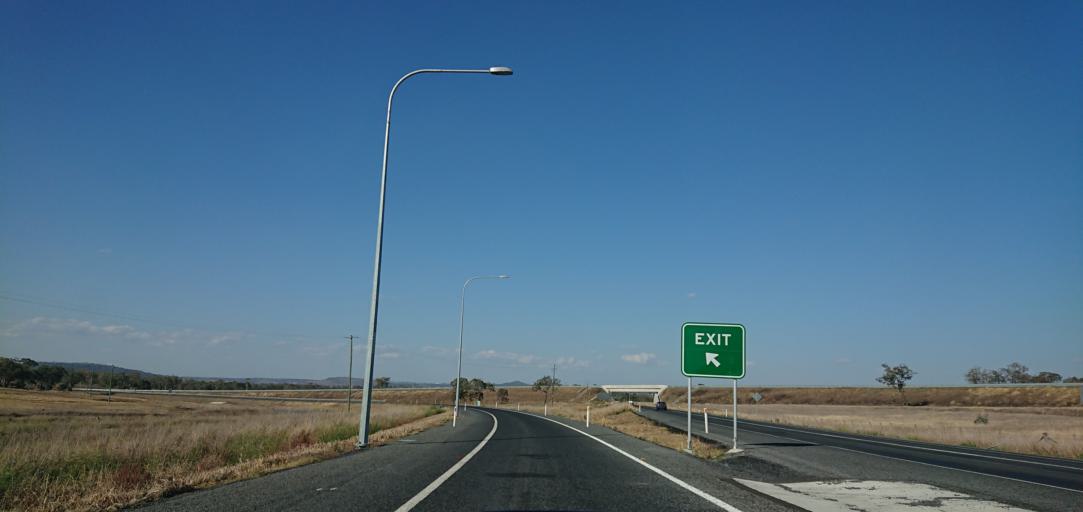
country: AU
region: Queensland
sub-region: Toowoomba
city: Westbrook
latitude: -27.6160
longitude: 151.7821
